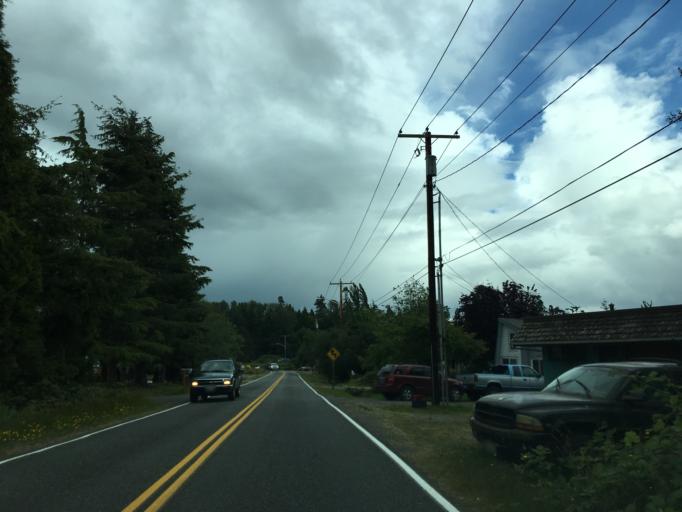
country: US
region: Washington
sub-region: Whatcom County
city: Birch Bay
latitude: 48.9437
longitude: -122.7632
